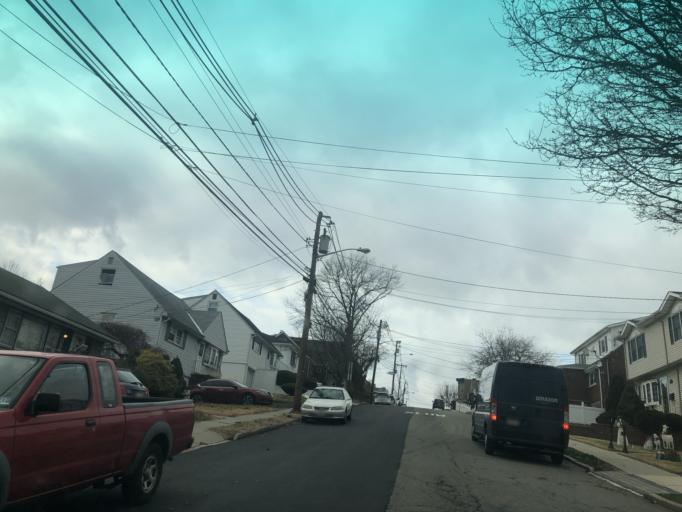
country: US
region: New Jersey
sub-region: Hudson County
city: Secaucus
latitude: 40.7972
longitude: -74.0535
